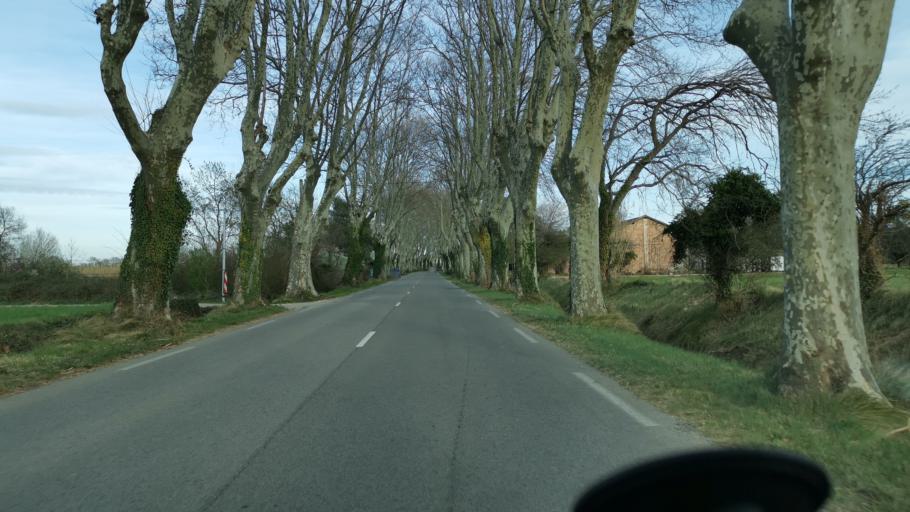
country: FR
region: Provence-Alpes-Cote d'Azur
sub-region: Departement des Bouches-du-Rhone
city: Saint-Martin-de-Crau
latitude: 43.6356
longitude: 4.7575
